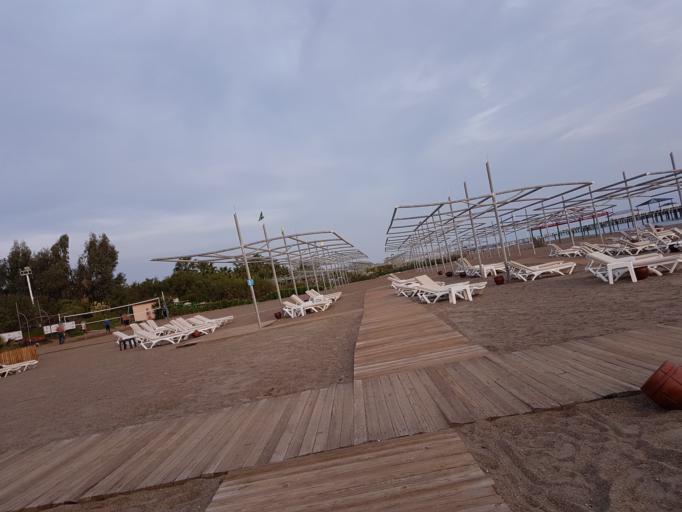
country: TR
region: Antalya
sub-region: Serik
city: Kumkoey
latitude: 36.8534
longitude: 30.8894
